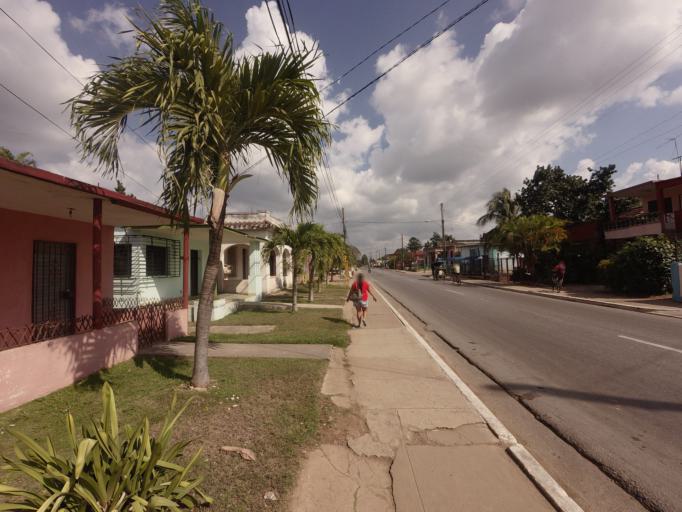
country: CU
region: Artemisa
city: Bauta
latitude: 22.9816
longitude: -82.5440
